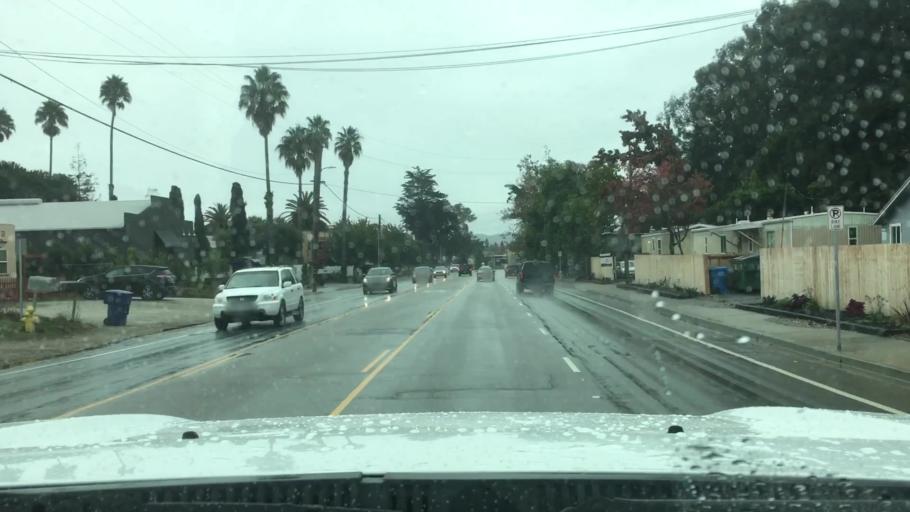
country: US
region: California
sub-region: San Luis Obispo County
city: San Luis Obispo
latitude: 35.2602
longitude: -120.6690
